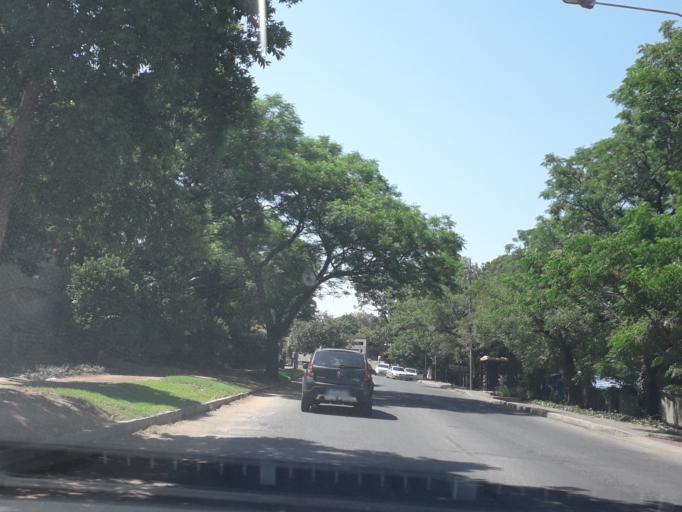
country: ZA
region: Gauteng
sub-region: City of Johannesburg Metropolitan Municipality
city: Johannesburg
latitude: -26.1308
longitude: 28.0247
